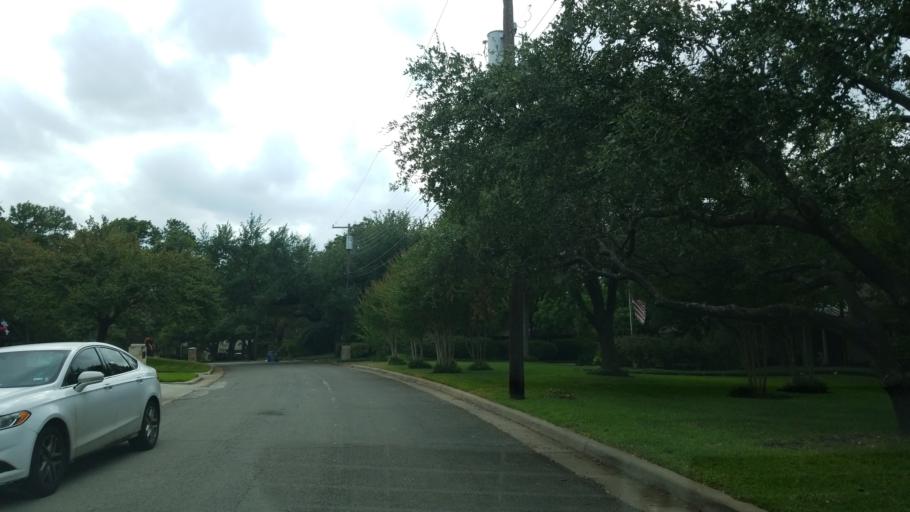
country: US
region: Texas
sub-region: Dallas County
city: Addison
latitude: 32.9381
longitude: -96.7822
